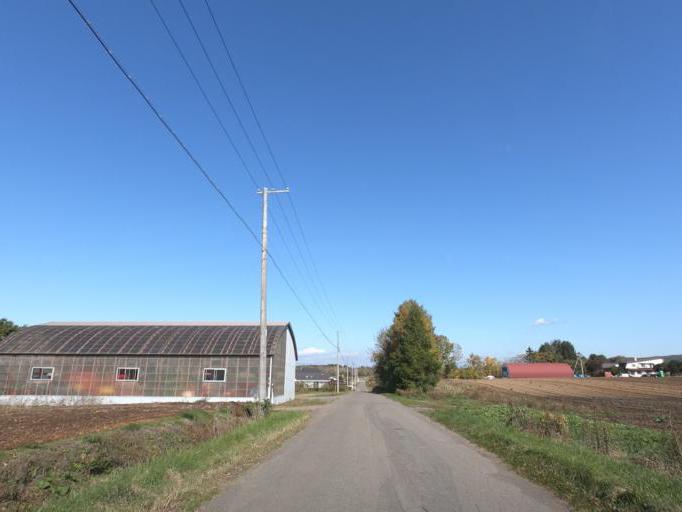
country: JP
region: Hokkaido
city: Otofuke
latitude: 43.0509
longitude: 143.2749
